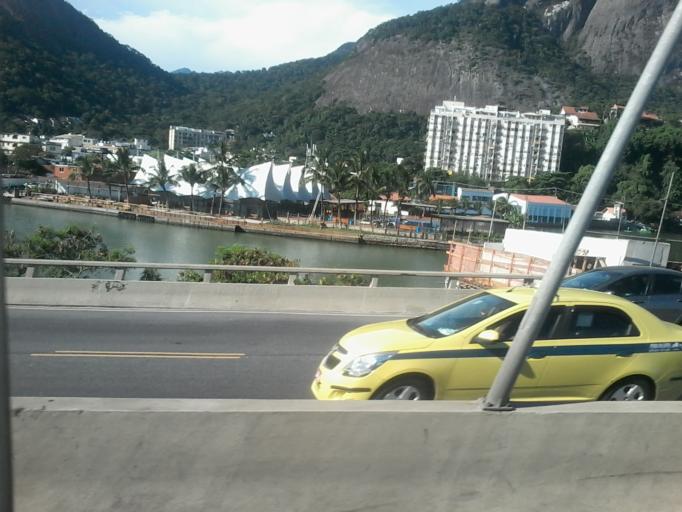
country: BR
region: Rio de Janeiro
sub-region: Rio De Janeiro
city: Rio de Janeiro
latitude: -23.0132
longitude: -43.2978
